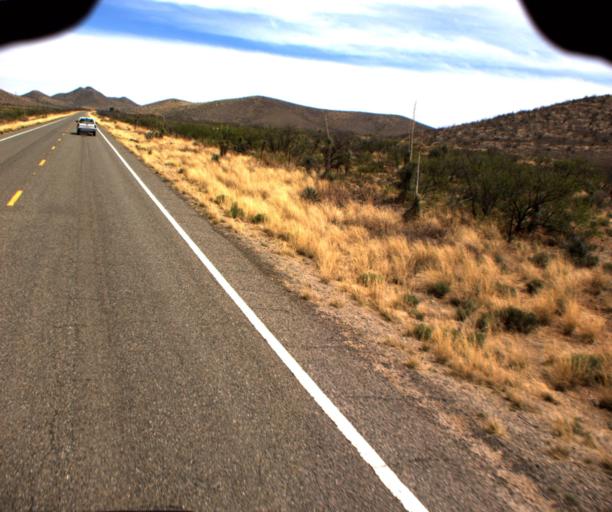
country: US
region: Arizona
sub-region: Cochise County
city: Willcox
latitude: 32.1890
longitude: -109.6869
